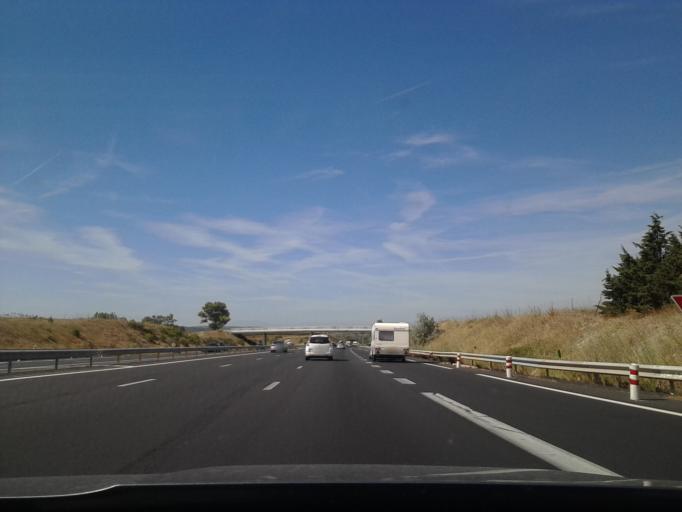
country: FR
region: Languedoc-Roussillon
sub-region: Departement de l'Herault
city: Lespignan
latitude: 43.2638
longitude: 3.1732
